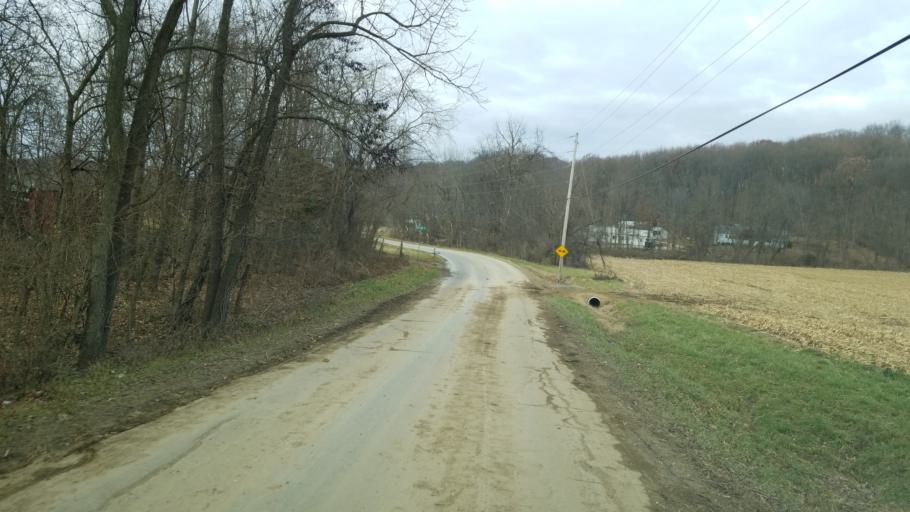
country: US
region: Ohio
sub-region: Highland County
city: Greenfield
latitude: 39.1842
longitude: -83.3562
